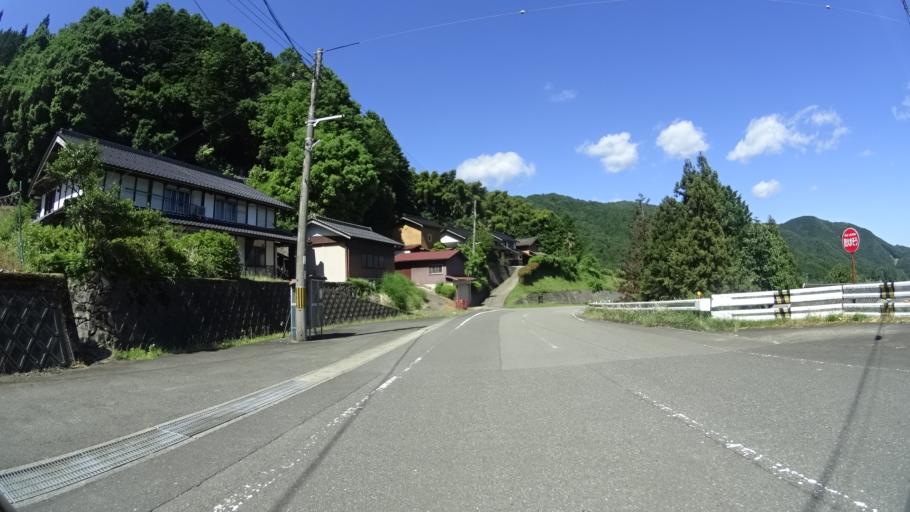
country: JP
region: Kyoto
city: Fukuchiyama
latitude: 35.4030
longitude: 135.0791
